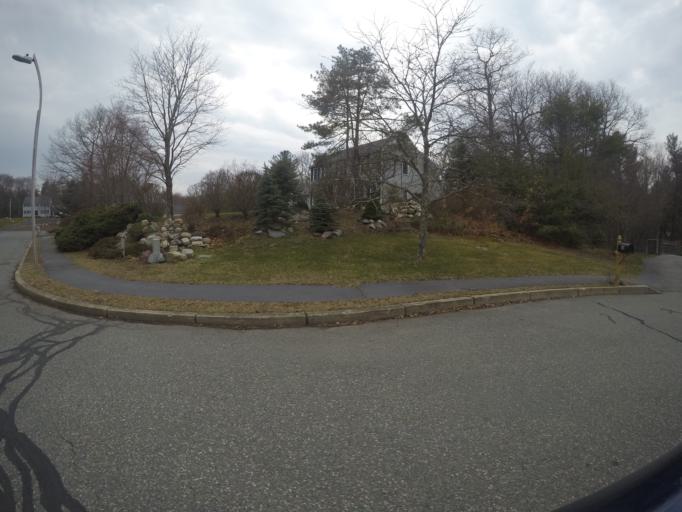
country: US
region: Massachusetts
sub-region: Norfolk County
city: Stoughton
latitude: 42.0814
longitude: -71.1017
